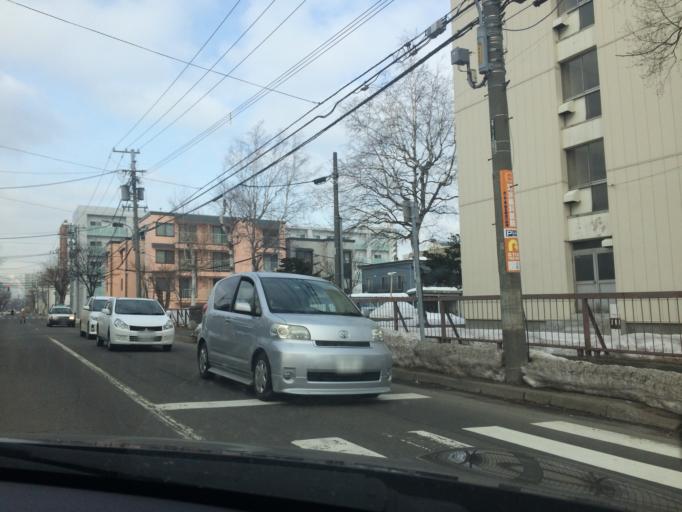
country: JP
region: Hokkaido
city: Sapporo
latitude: 43.0763
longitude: 141.3599
